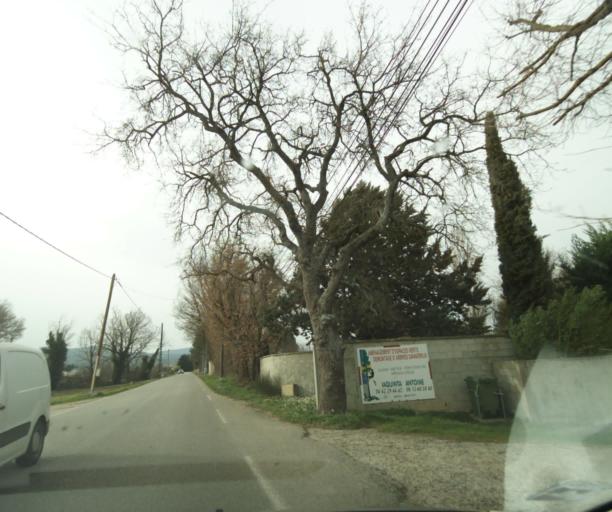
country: FR
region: Provence-Alpes-Cote d'Azur
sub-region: Departement des Bouches-du-Rhone
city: Trets
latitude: 43.4611
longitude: 5.6992
